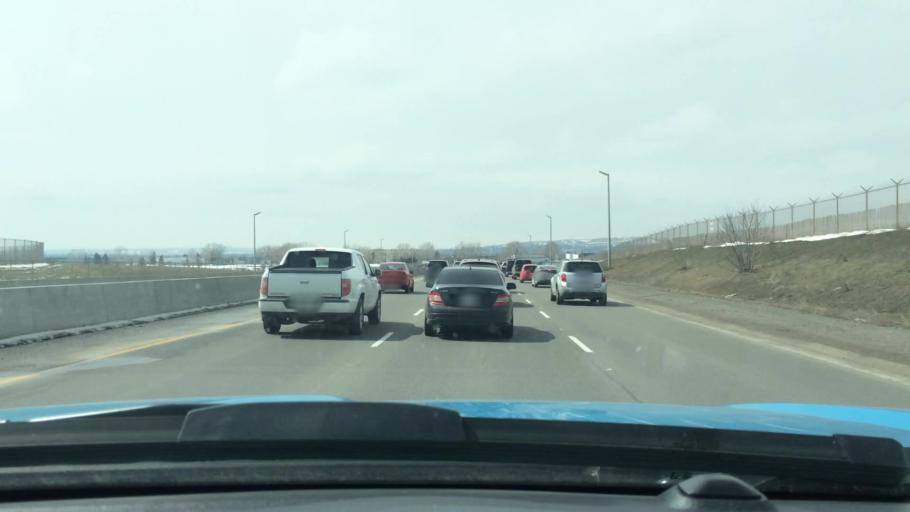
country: CA
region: Alberta
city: Calgary
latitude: 51.0931
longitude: -114.0176
